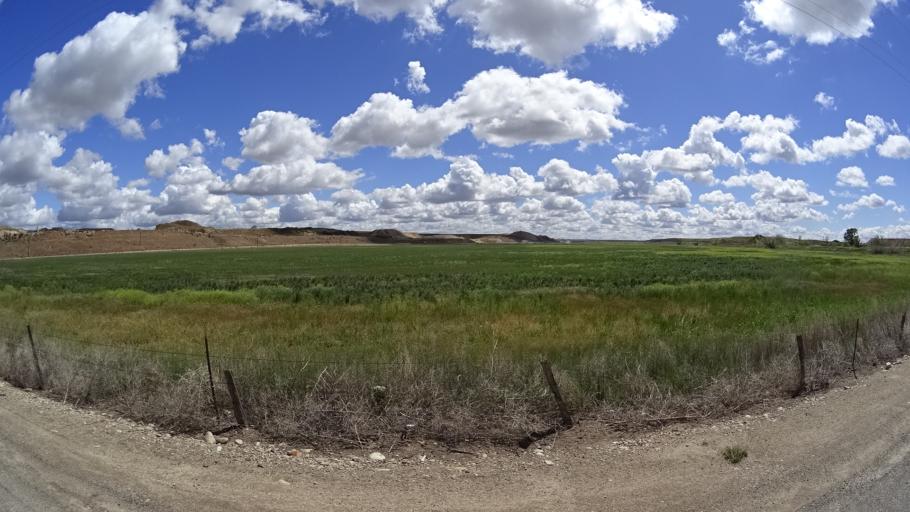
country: US
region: Idaho
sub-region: Ada County
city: Garden City
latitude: 43.4906
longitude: -116.2744
